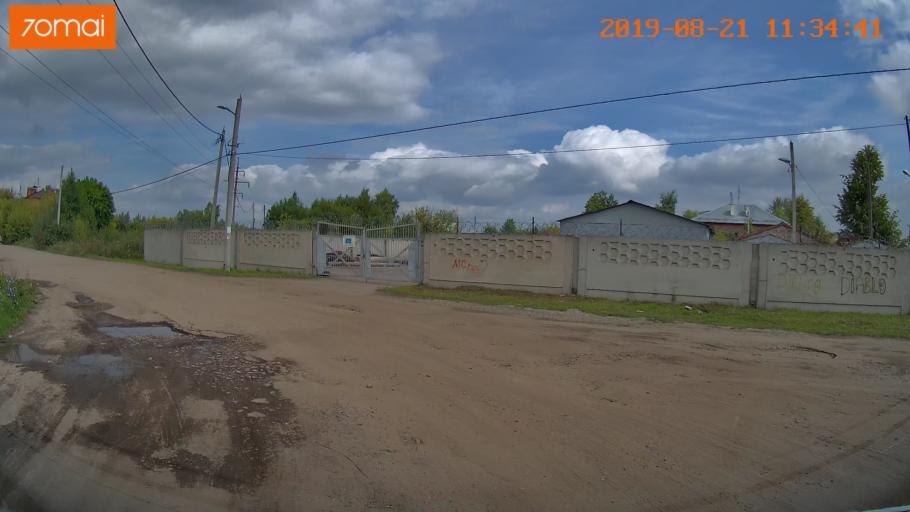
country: RU
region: Ivanovo
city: Novo-Talitsy
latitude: 56.9883
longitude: 40.9120
